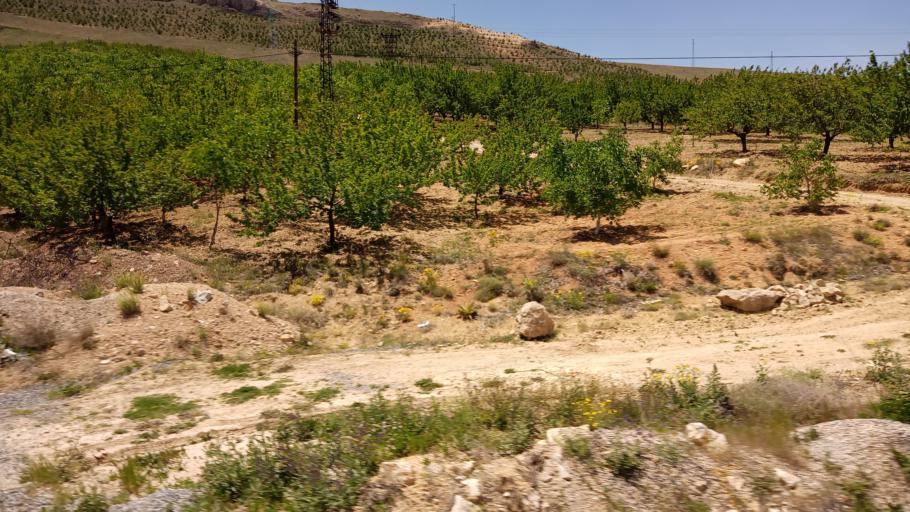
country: TR
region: Malatya
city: Darende
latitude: 38.6152
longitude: 37.4566
